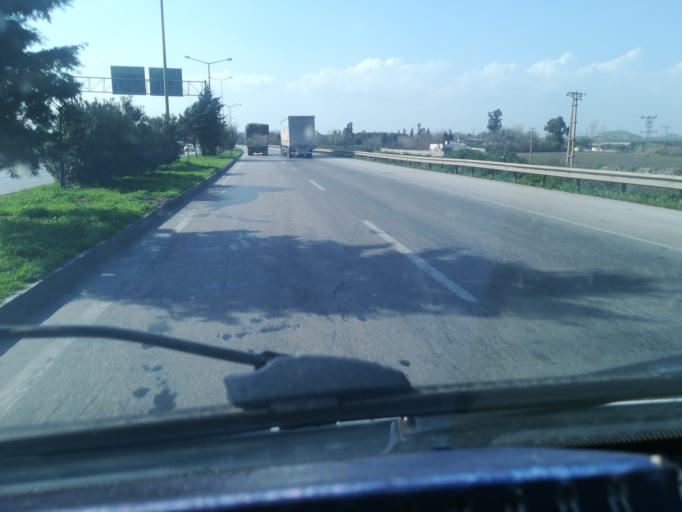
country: TR
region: Osmaniye
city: Toprakkale
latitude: 37.0746
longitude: 36.0833
